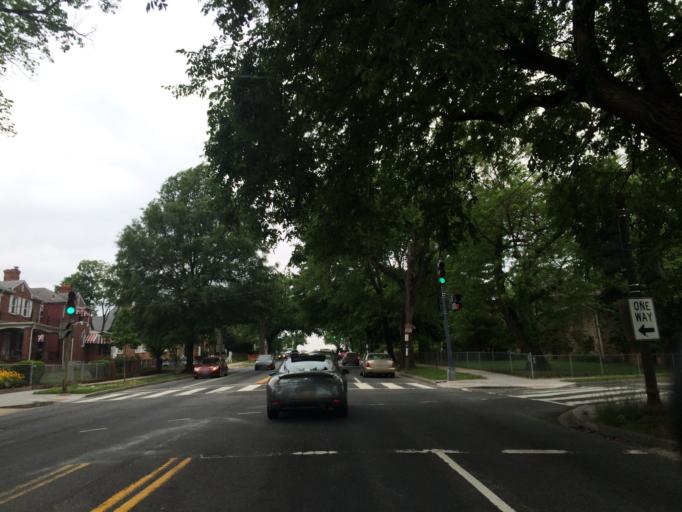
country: US
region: Maryland
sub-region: Prince George's County
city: Chillum
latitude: 38.9565
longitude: -77.0091
